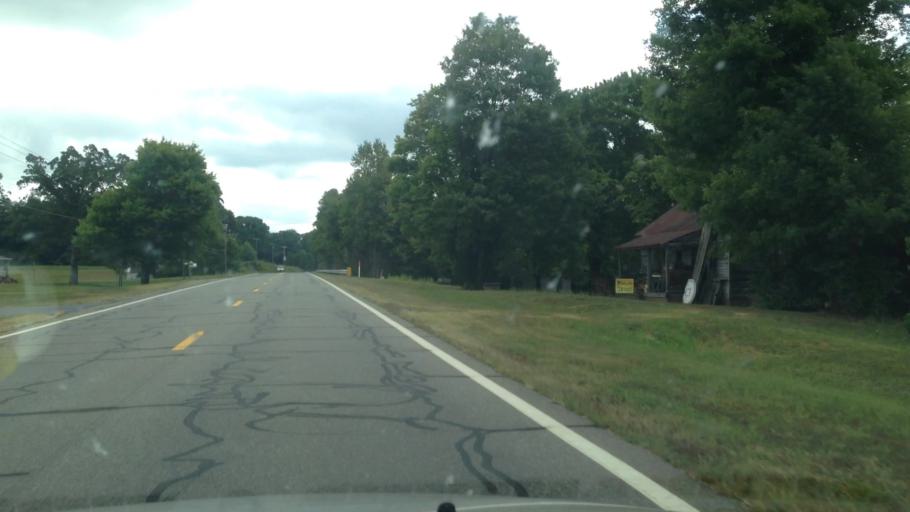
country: US
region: North Carolina
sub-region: Rockingham County
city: Madison
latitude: 36.3814
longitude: -79.9217
